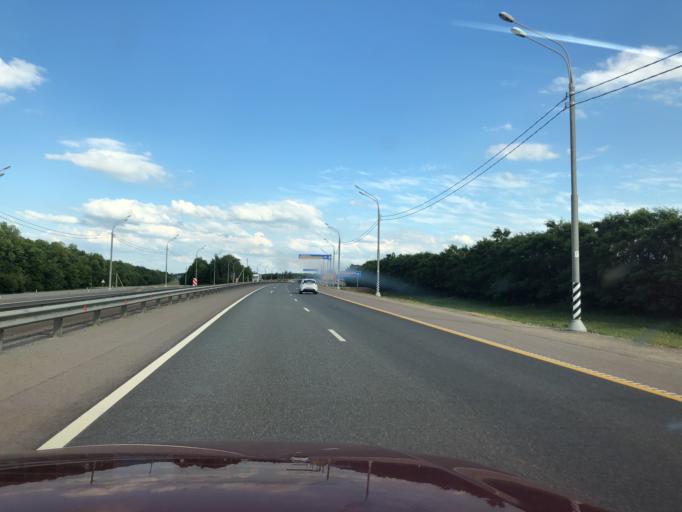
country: RU
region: Lipetsk
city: Zadonsk
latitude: 52.4389
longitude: 38.8086
